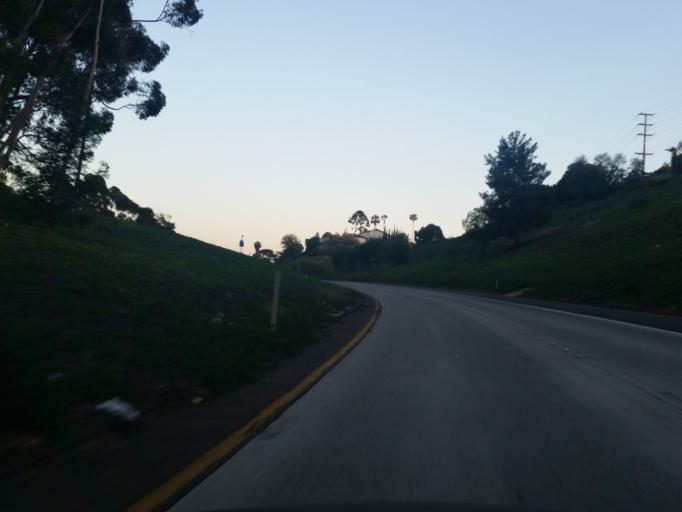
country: US
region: California
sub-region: San Diego County
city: San Diego
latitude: 32.7370
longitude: -117.1154
